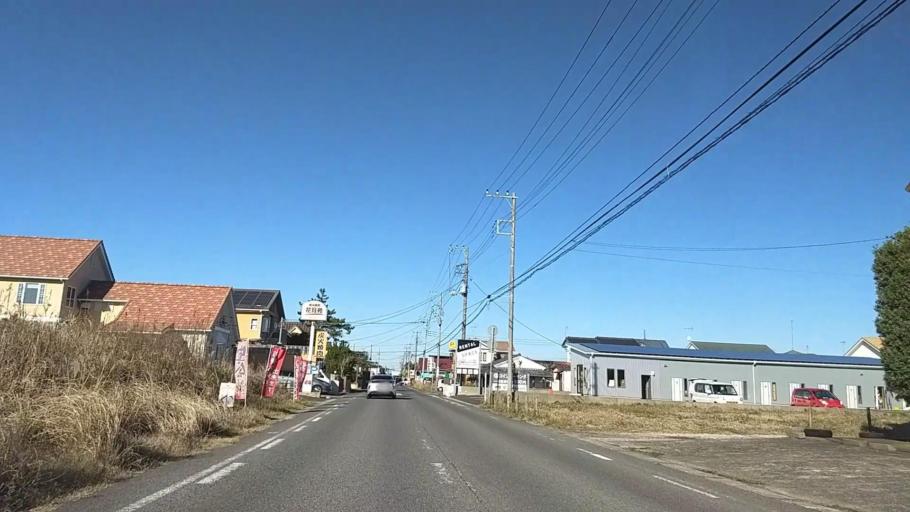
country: JP
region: Chiba
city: Mobara
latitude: 35.3682
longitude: 140.3878
